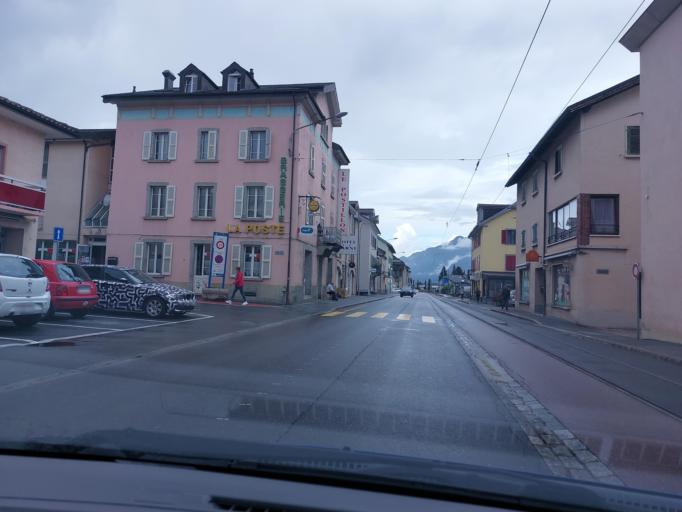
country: CH
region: Valais
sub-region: Monthey District
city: Collombey
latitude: 46.2682
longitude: 6.9459
